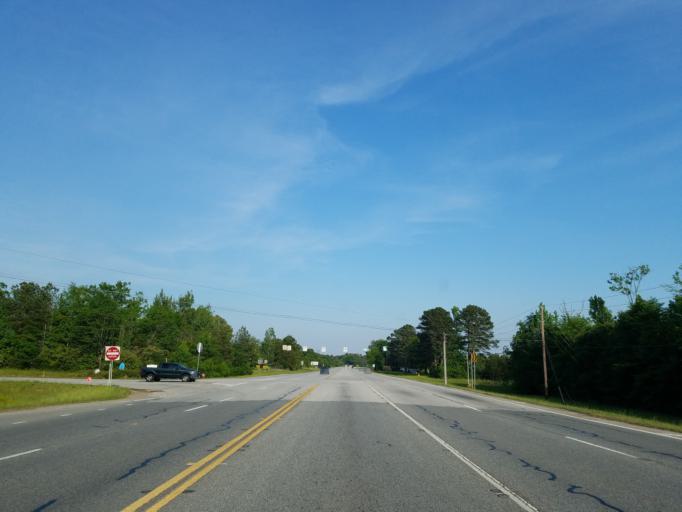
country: US
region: Georgia
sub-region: Floyd County
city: Shannon
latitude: 34.3924
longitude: -85.1902
